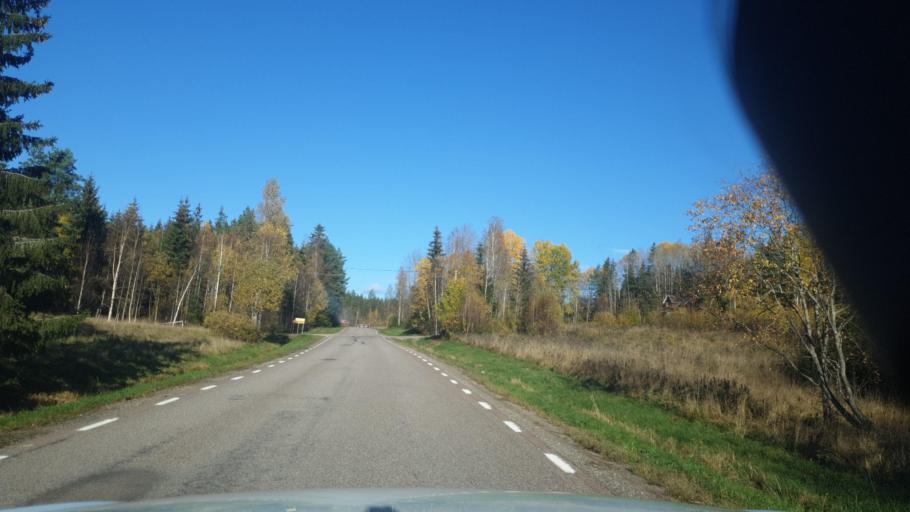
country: SE
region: Vaermland
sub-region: Arvika Kommun
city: Arvika
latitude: 59.6179
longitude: 12.7877
